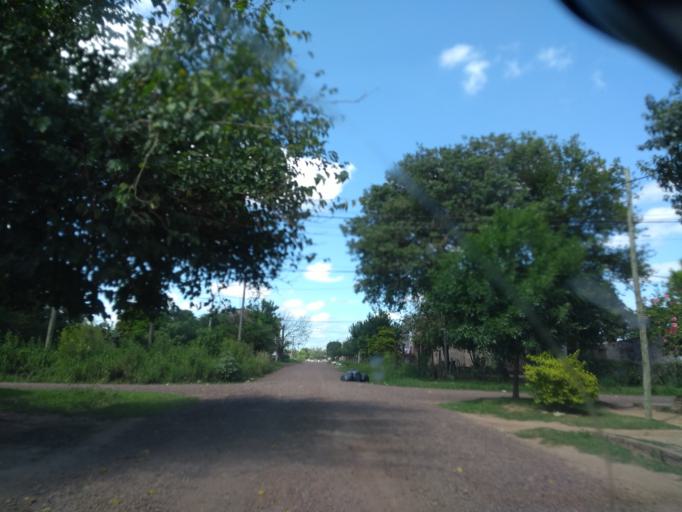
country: AR
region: Chaco
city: Fontana
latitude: -27.4069
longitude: -59.0417
